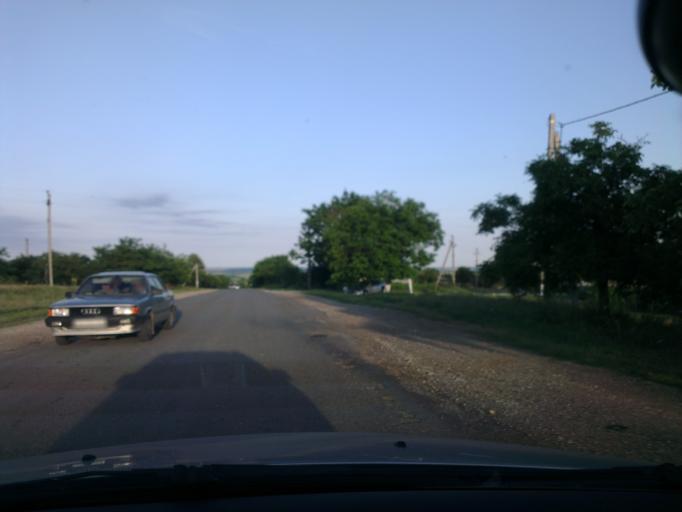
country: MD
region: Cantemir
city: Visniovca
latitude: 46.3595
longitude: 28.3996
